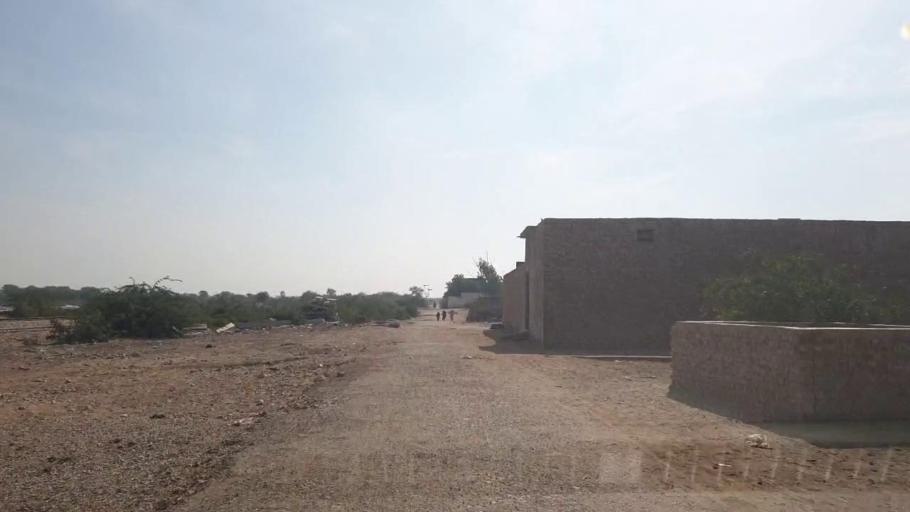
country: PK
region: Sindh
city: Hala
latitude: 25.7479
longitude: 68.2942
